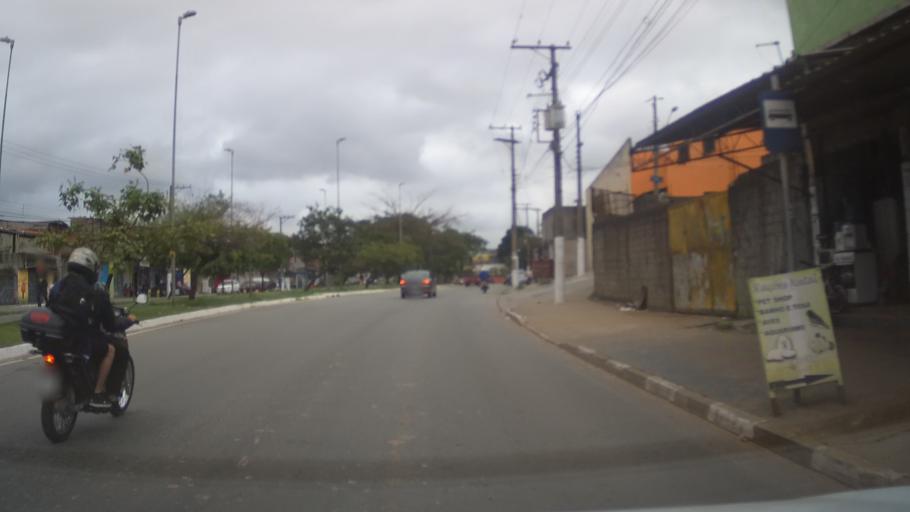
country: BR
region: Sao Paulo
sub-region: Guarulhos
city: Guarulhos
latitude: -23.4090
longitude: -46.4512
